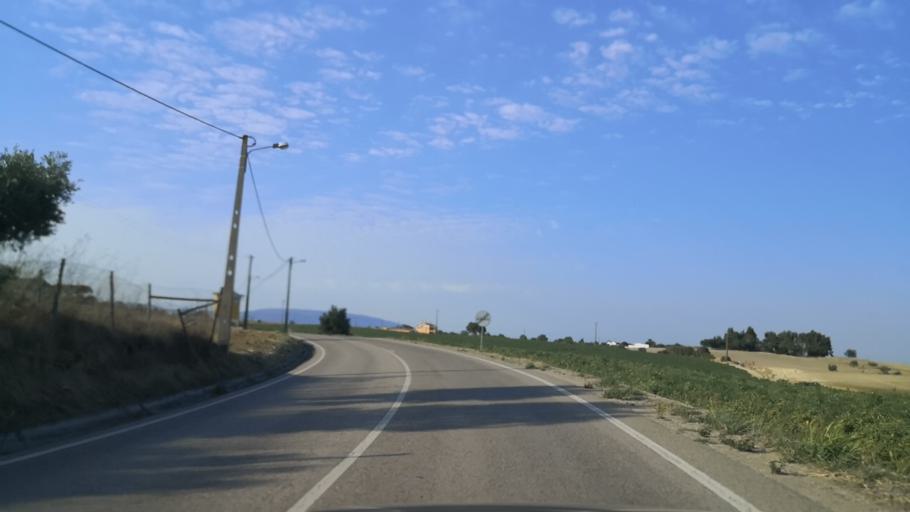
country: PT
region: Santarem
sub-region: Santarem
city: Santarem
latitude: 39.3419
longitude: -8.6611
